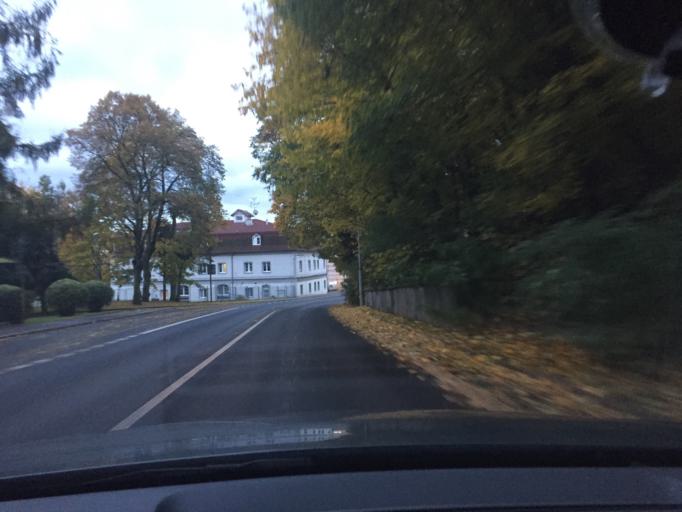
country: CZ
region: Ustecky
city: Dubi
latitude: 50.6777
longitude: 13.7908
